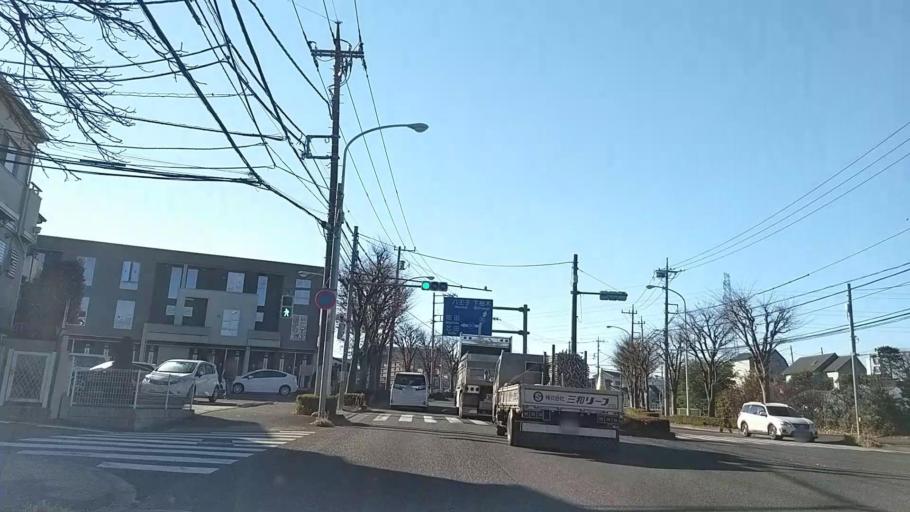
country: JP
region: Tokyo
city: Hino
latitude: 35.6454
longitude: 139.4351
